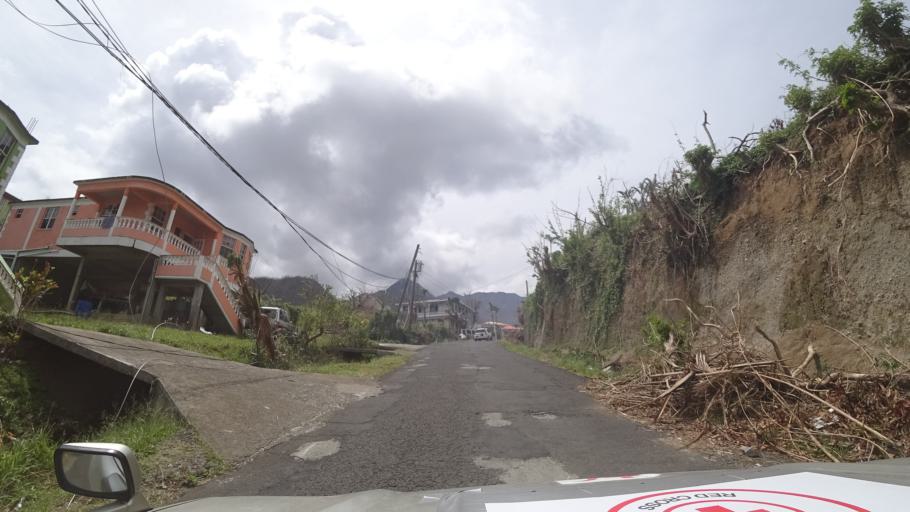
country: DM
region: Saint Patrick
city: Berekua
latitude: 15.2454
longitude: -61.3164
